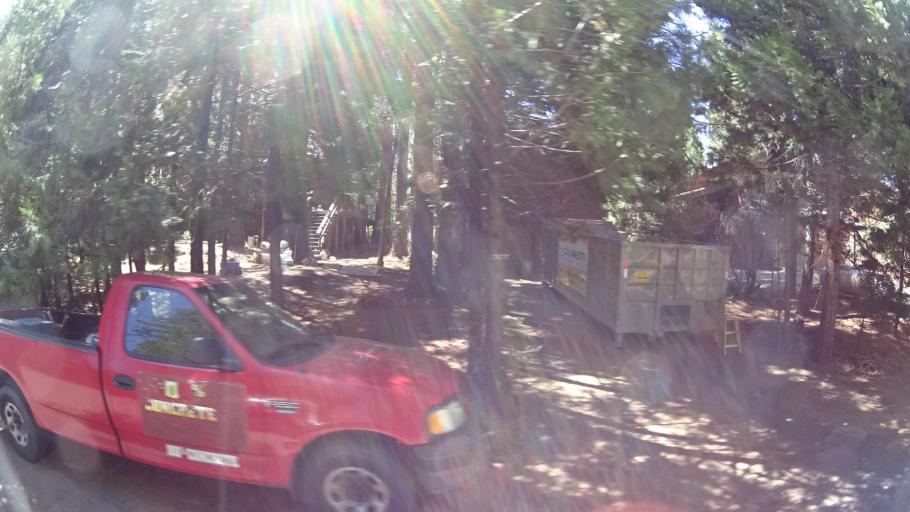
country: US
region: California
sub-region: Calaveras County
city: Arnold
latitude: 38.2254
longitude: -120.3419
